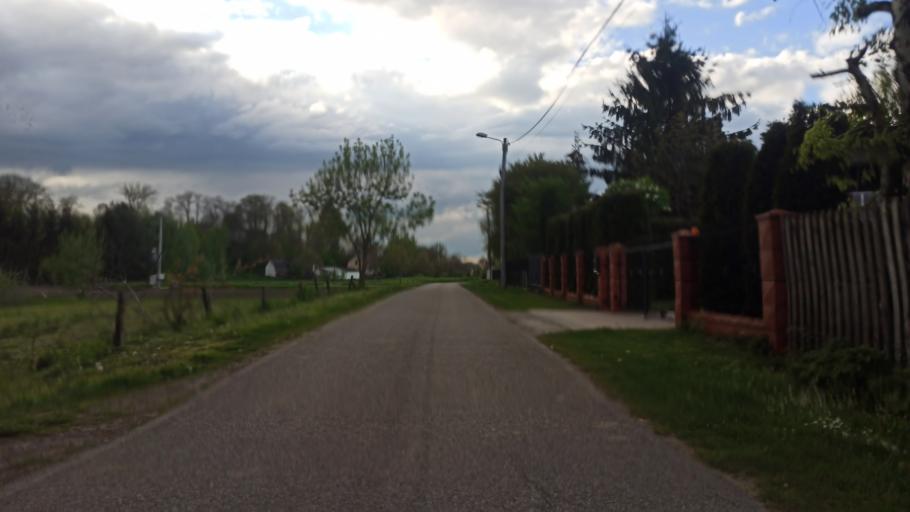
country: PL
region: Subcarpathian Voivodeship
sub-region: Powiat jaroslawski
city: Sosnica
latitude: 49.9237
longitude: 22.8594
